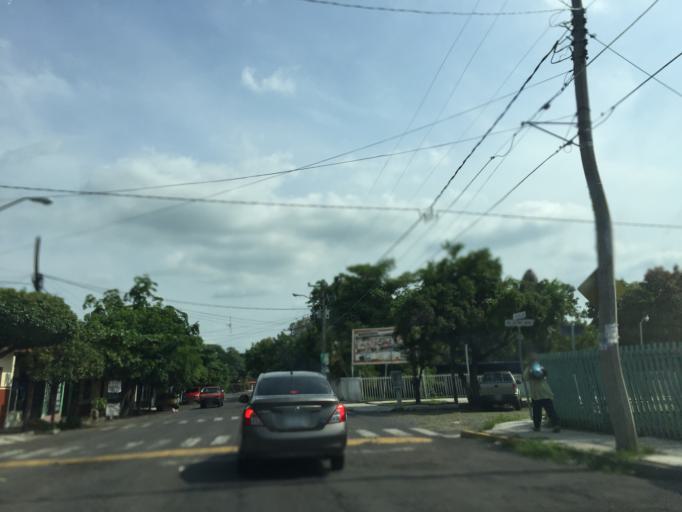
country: MX
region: Colima
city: Colima
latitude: 19.2326
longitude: -103.7324
